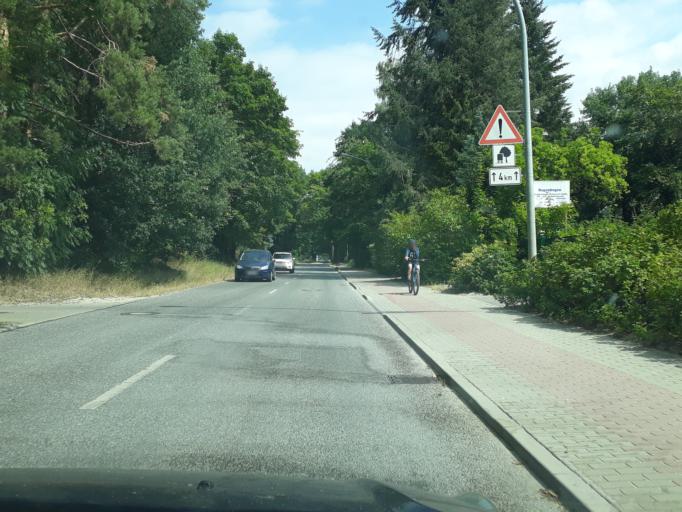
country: DE
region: Brandenburg
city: Stahnsdorf
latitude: 52.3664
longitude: 13.2096
